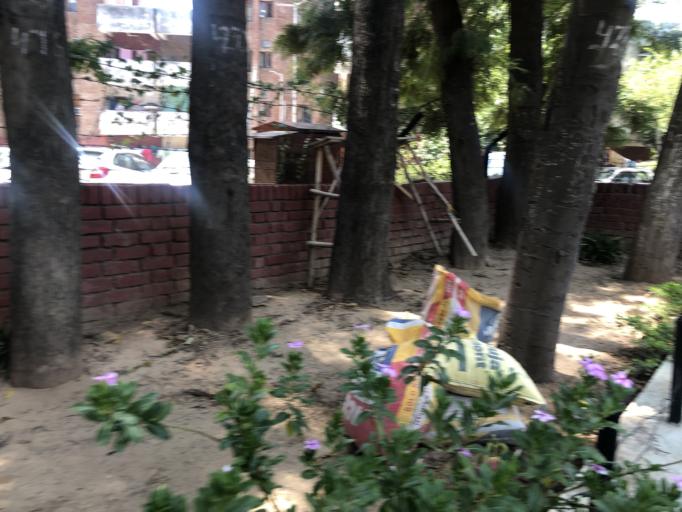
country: IN
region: Chandigarh
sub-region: Chandigarh
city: Chandigarh
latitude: 30.7121
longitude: 76.7733
